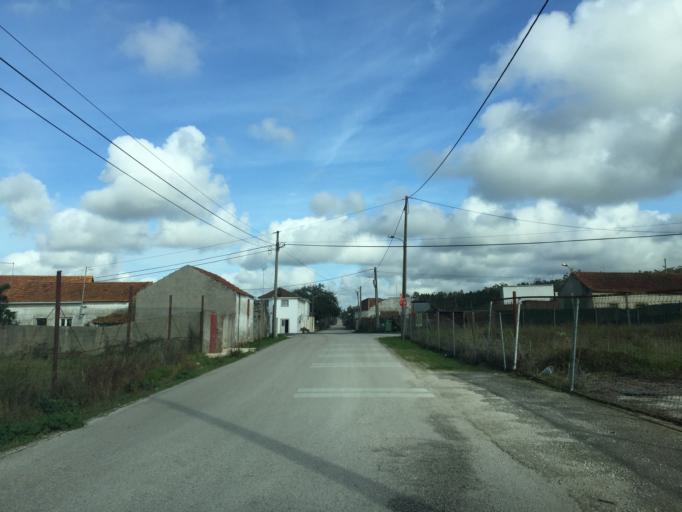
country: PT
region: Leiria
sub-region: Alcobaca
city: Benedita
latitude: 39.4460
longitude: -8.9522
